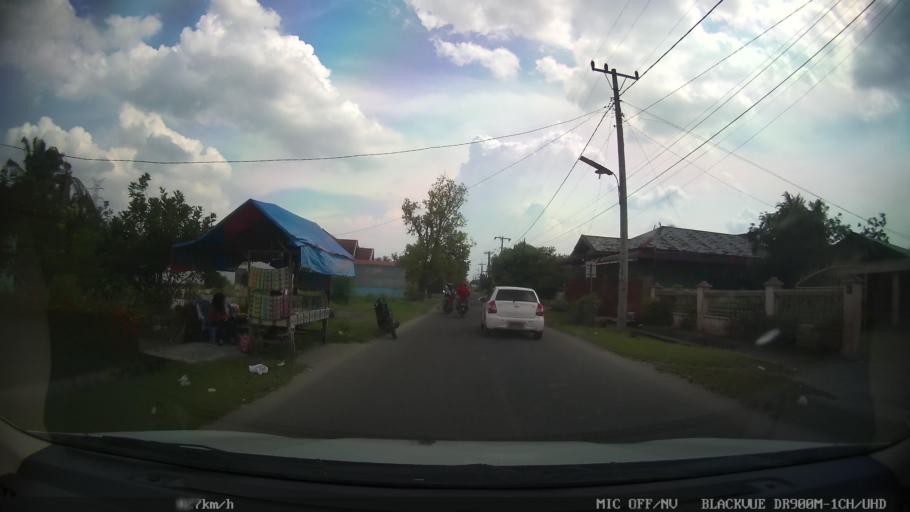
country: ID
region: North Sumatra
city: Binjai
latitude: 3.6271
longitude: 98.5014
